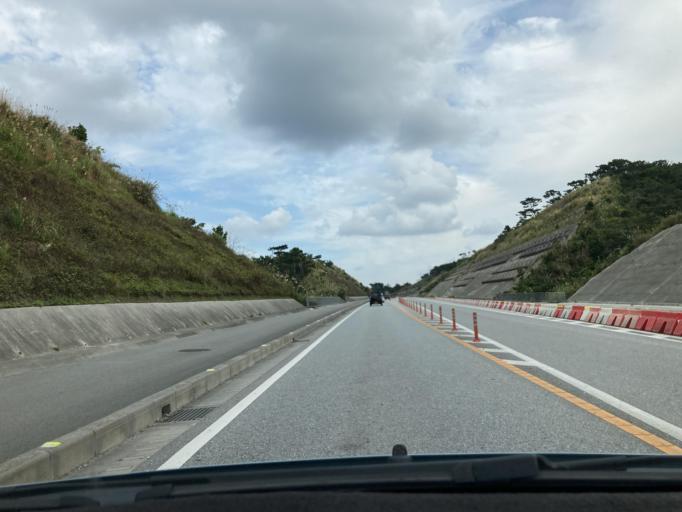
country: JP
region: Okinawa
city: Ishikawa
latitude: 26.4694
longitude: 127.8342
